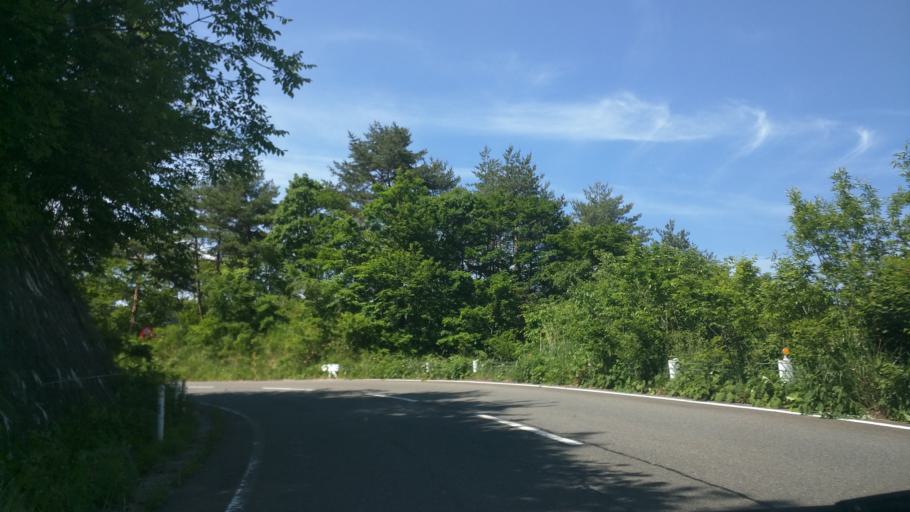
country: JP
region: Fukushima
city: Kitakata
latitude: 37.3763
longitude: 139.8813
